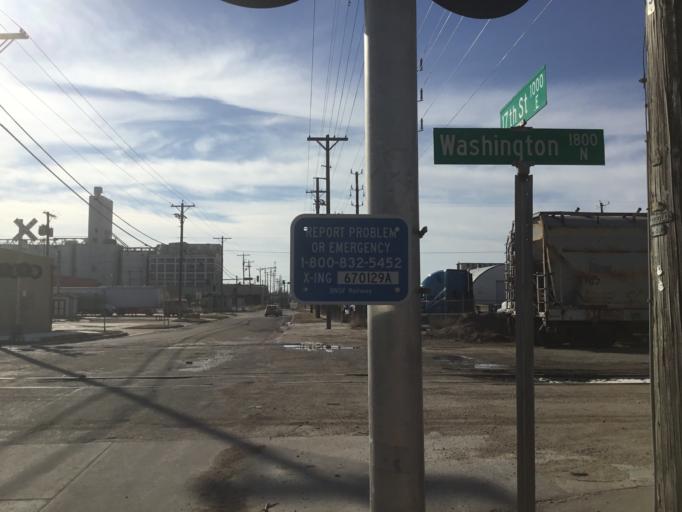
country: US
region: Kansas
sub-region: Sedgwick County
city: Wichita
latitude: 37.7154
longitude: -97.3263
